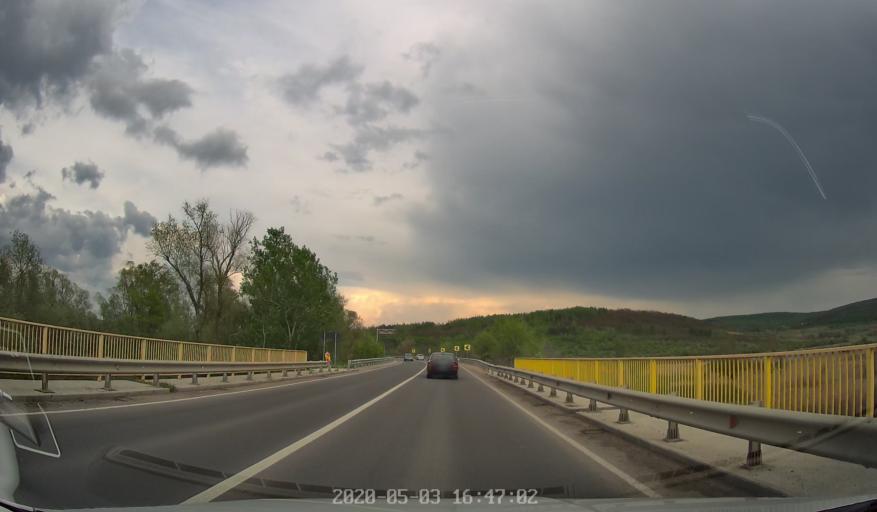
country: MD
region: Stinga Nistrului
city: Bucovat
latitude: 47.1798
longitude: 28.4698
